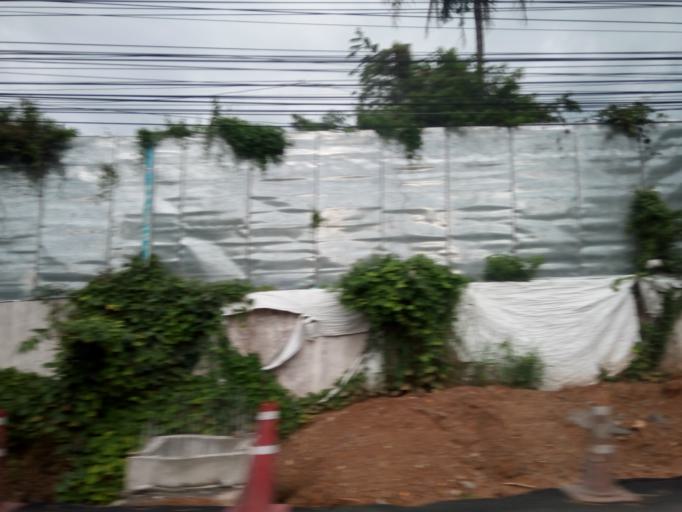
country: TH
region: Phuket
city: Thalang
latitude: 8.1000
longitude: 98.3354
